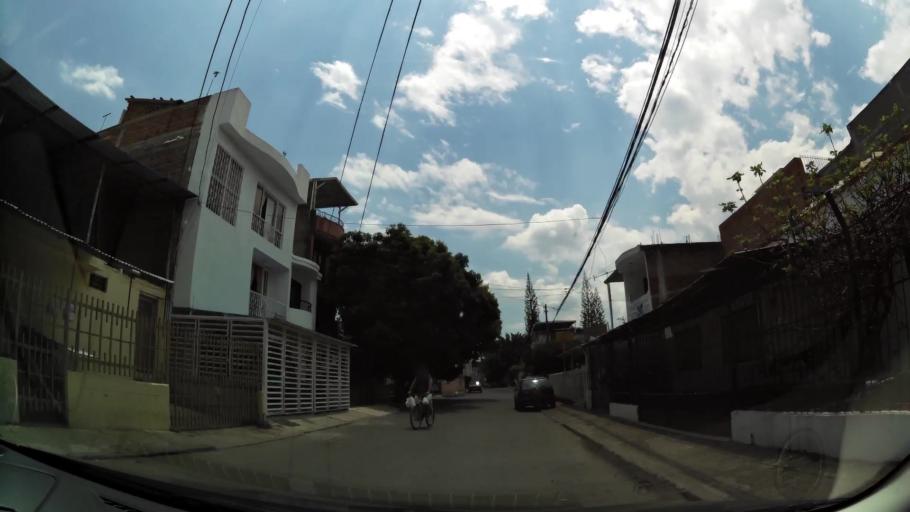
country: CO
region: Valle del Cauca
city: Cali
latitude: 3.4120
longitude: -76.5346
